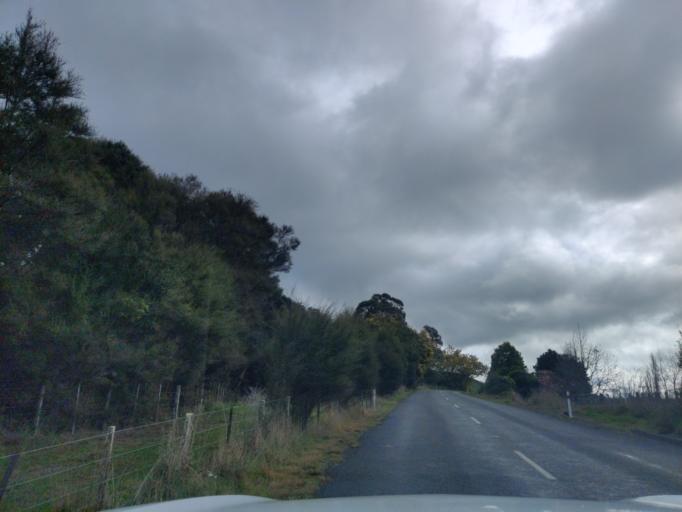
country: NZ
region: Manawatu-Wanganui
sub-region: Palmerston North City
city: Palmerston North
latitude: -40.1927
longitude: 175.7820
